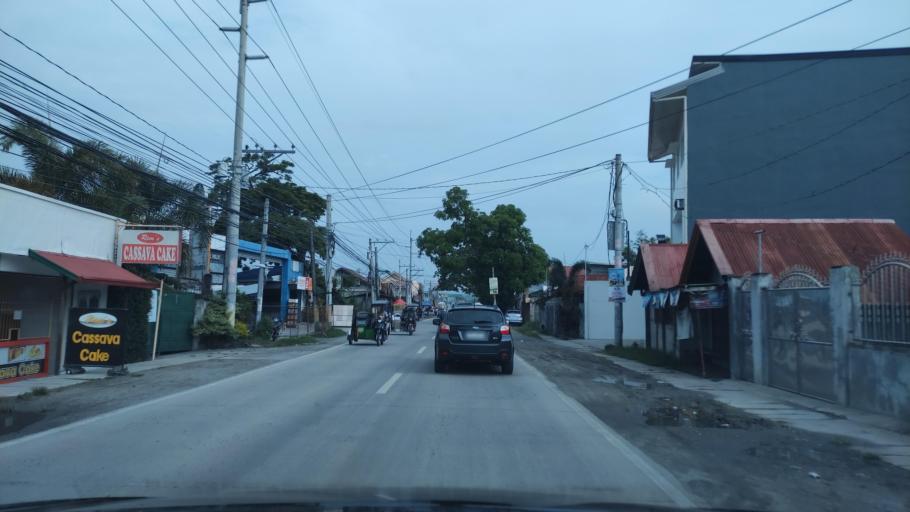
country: PH
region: Central Luzon
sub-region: Province of Pampanga
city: Arayat
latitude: 15.1444
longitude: 120.7700
